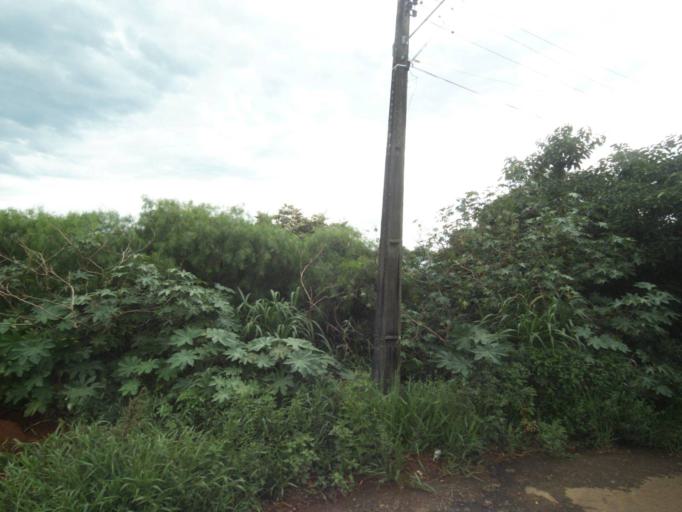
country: BR
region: Parana
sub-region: Guaraniacu
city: Guaraniacu
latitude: -25.1036
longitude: -52.8689
